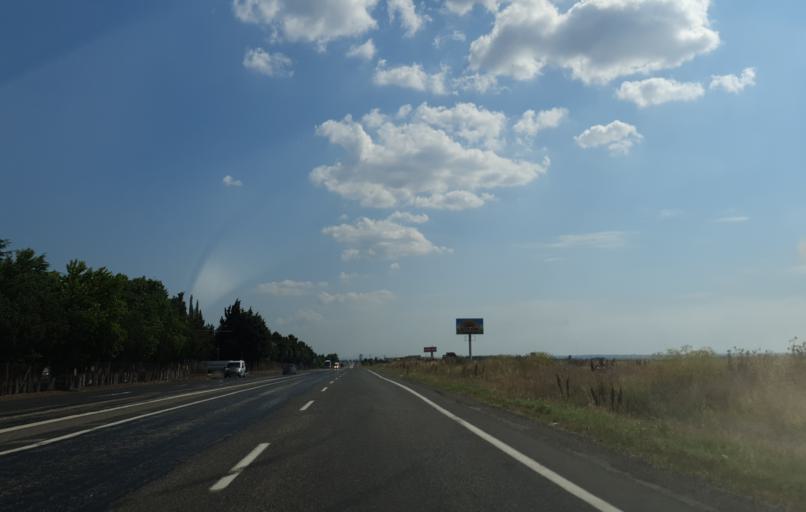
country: TR
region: Kirklareli
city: Buyukkaristiran
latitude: 41.2804
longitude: 27.5566
